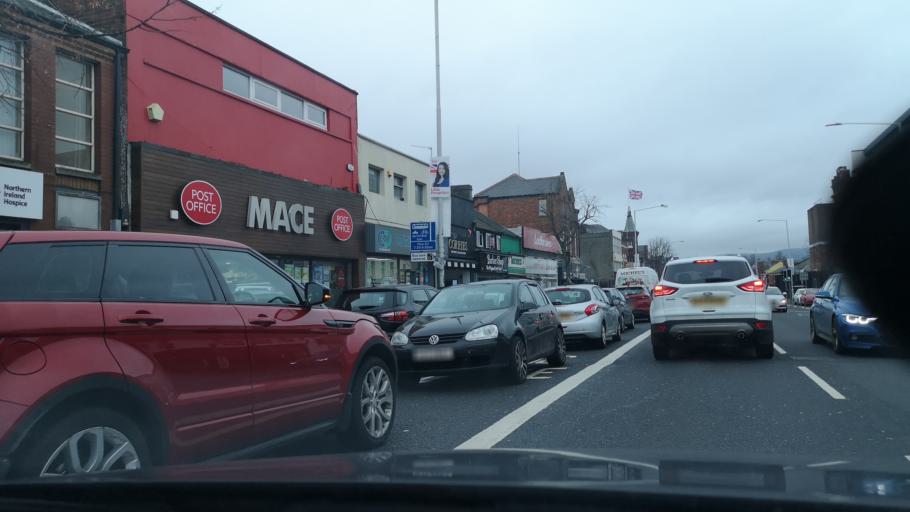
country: GB
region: Northern Ireland
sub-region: City of Belfast
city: Belfast
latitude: 54.5755
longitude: -5.9170
